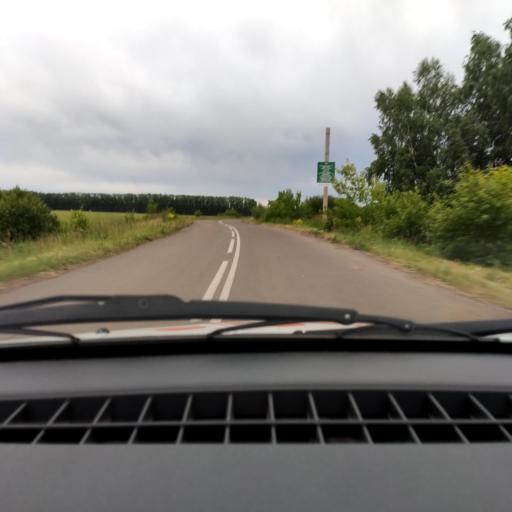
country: RU
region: Bashkortostan
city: Avdon
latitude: 54.5397
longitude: 55.7617
